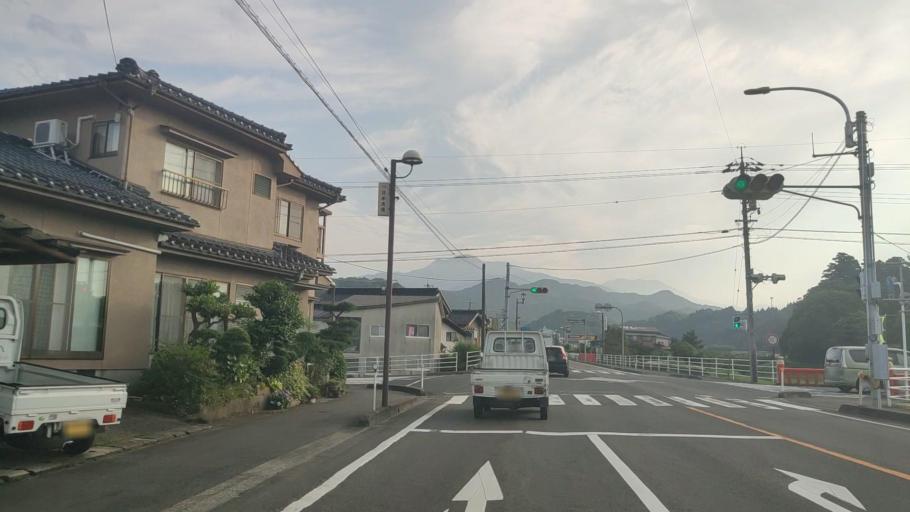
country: JP
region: Tottori
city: Kurayoshi
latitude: 35.3661
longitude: 133.7596
